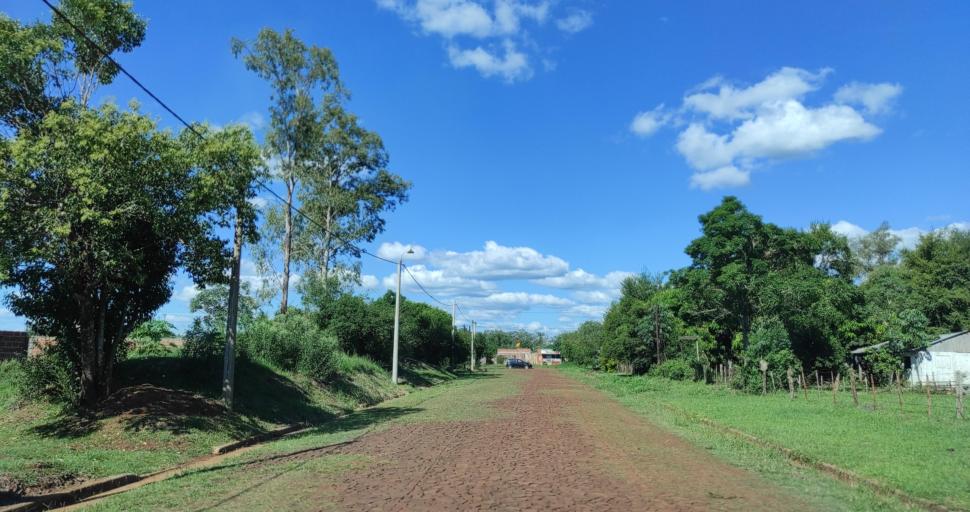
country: AR
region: Misiones
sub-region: Departamento de Candelaria
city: Candelaria
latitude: -27.4603
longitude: -55.7356
